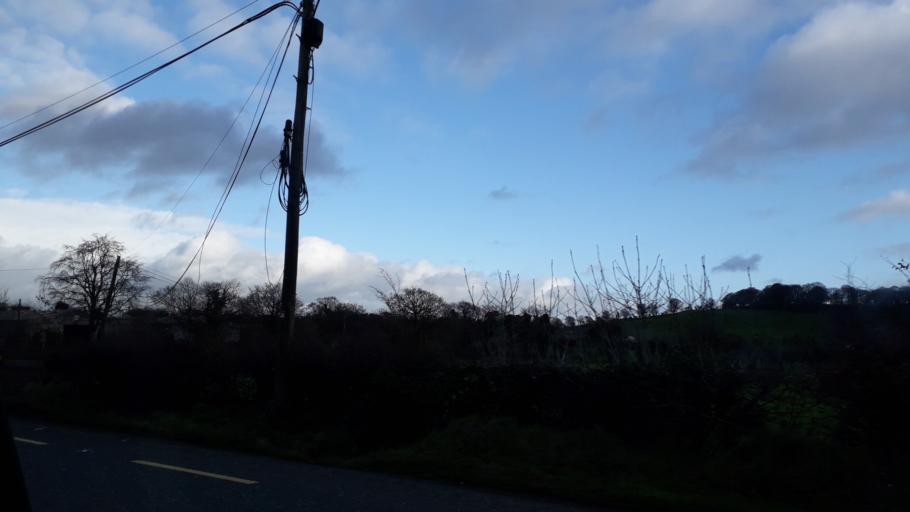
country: IE
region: Leinster
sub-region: An Mhi
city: Slane
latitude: 53.7618
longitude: -6.4955
